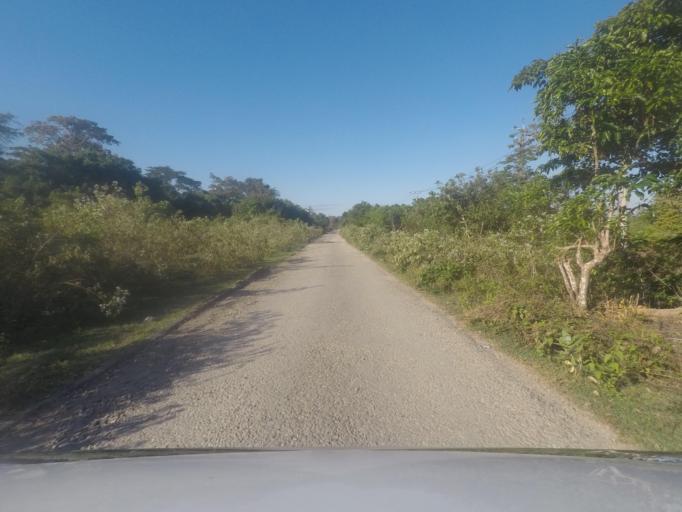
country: TL
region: Lautem
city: Lospalos
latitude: -8.4091
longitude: 127.1681
